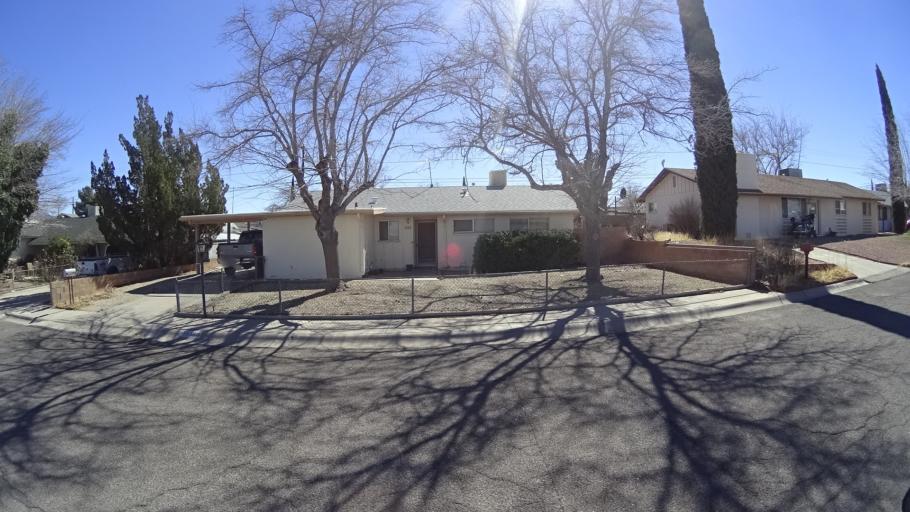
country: US
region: Arizona
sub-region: Mohave County
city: Kingman
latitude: 35.1981
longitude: -114.0318
